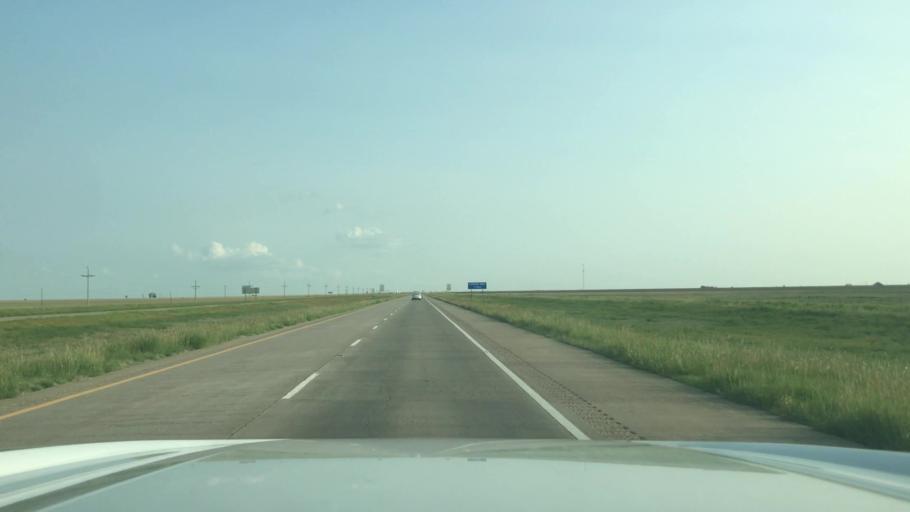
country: US
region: Texas
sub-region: Randall County
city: Canyon
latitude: 34.8695
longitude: -101.8490
